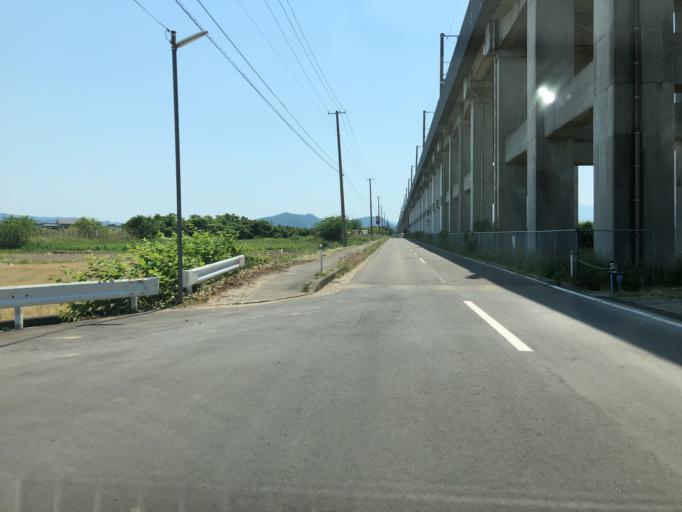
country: JP
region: Fukushima
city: Hobaramachi
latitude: 37.8198
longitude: 140.4909
